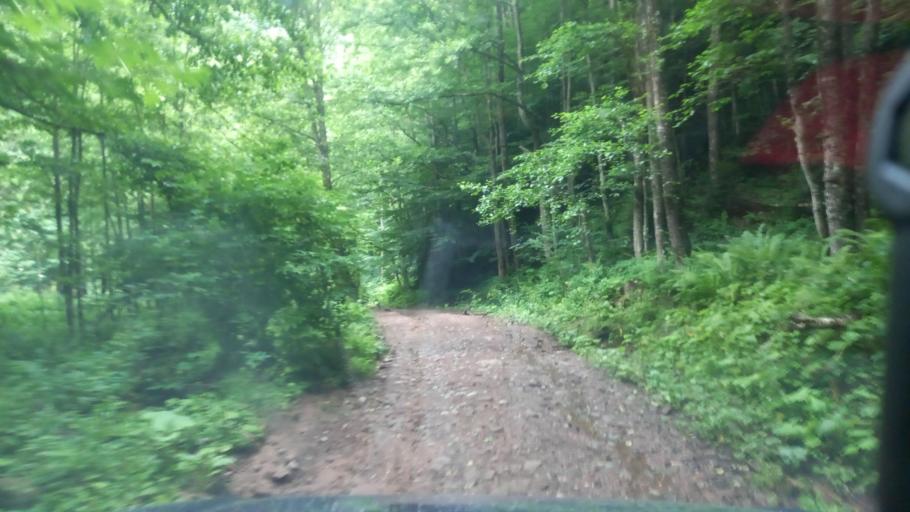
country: RU
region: Karachayevo-Cherkesiya
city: Kurdzhinovo
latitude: 43.8137
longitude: 40.8810
